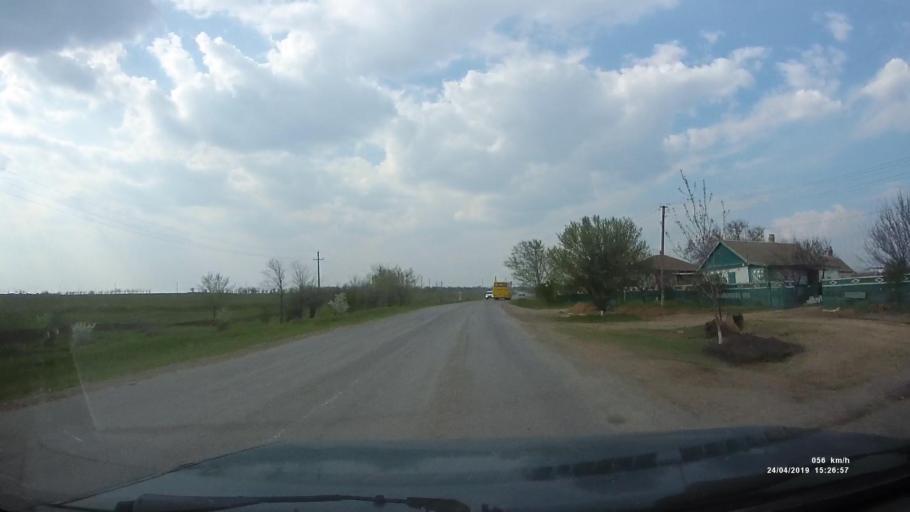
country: RU
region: Rostov
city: Remontnoye
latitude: 46.5604
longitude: 43.0297
